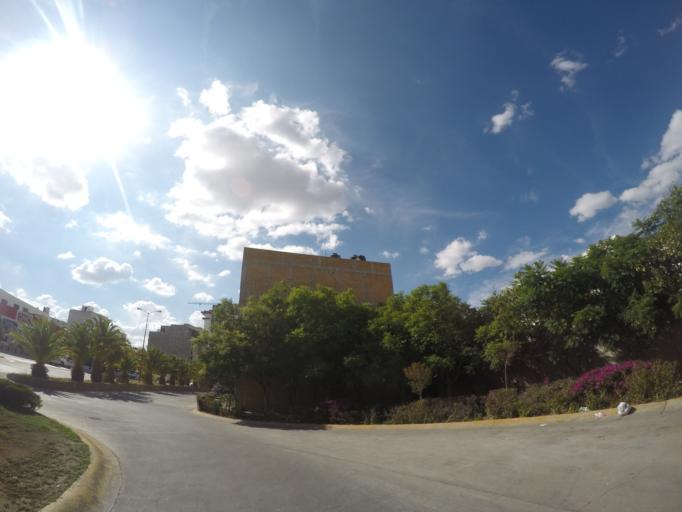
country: MX
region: San Luis Potosi
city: Escalerillas
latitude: 22.1215
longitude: -101.0322
